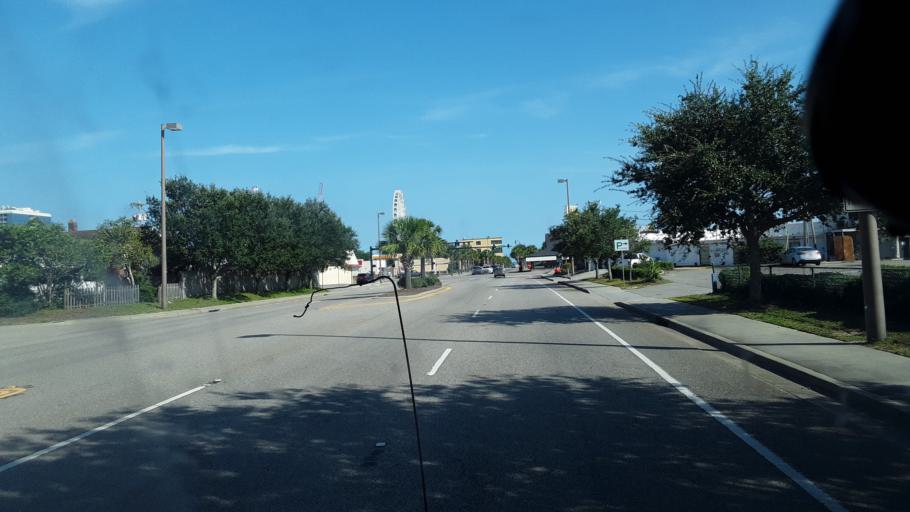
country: US
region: South Carolina
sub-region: Horry County
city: Myrtle Beach
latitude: 33.6964
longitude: -78.8814
